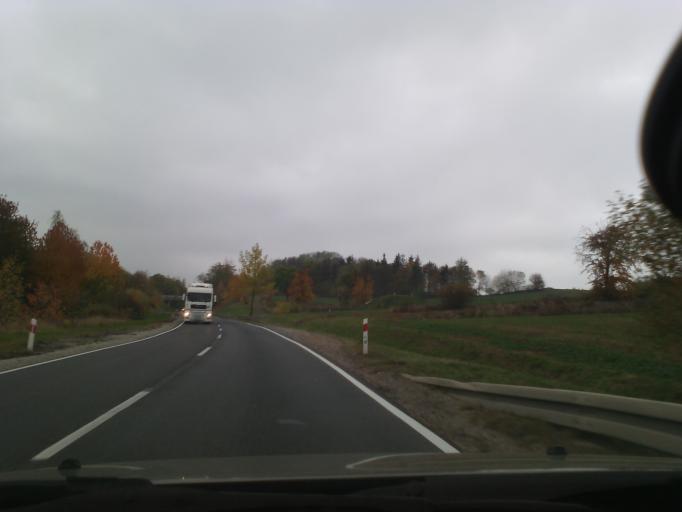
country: PL
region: Lower Silesian Voivodeship
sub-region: Powiat walbrzyski
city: Stare Bogaczowice
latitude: 50.9129
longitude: 16.2335
